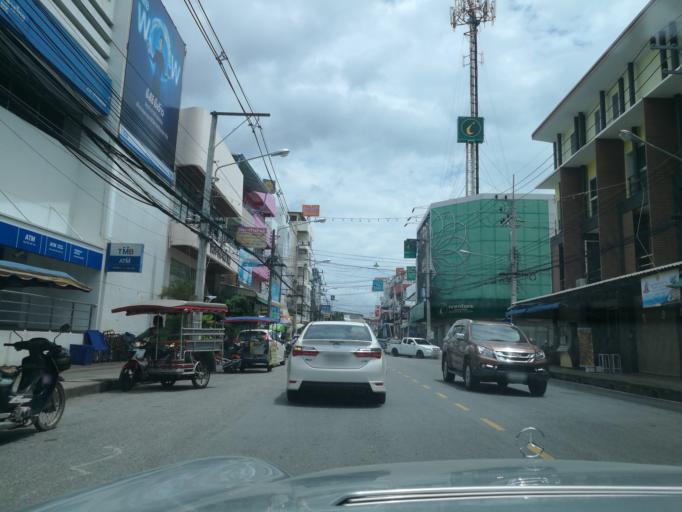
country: TH
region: Prachuap Khiri Khan
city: Prachuap Khiri Khan
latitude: 11.8017
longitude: 99.7982
